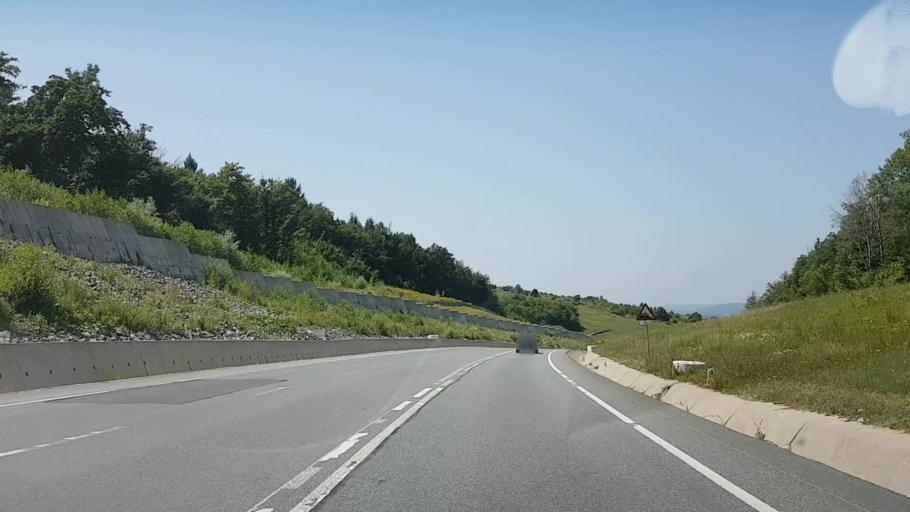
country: RO
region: Cluj
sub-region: Comuna Feleacu
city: Feleacu
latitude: 46.7197
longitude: 23.6520
